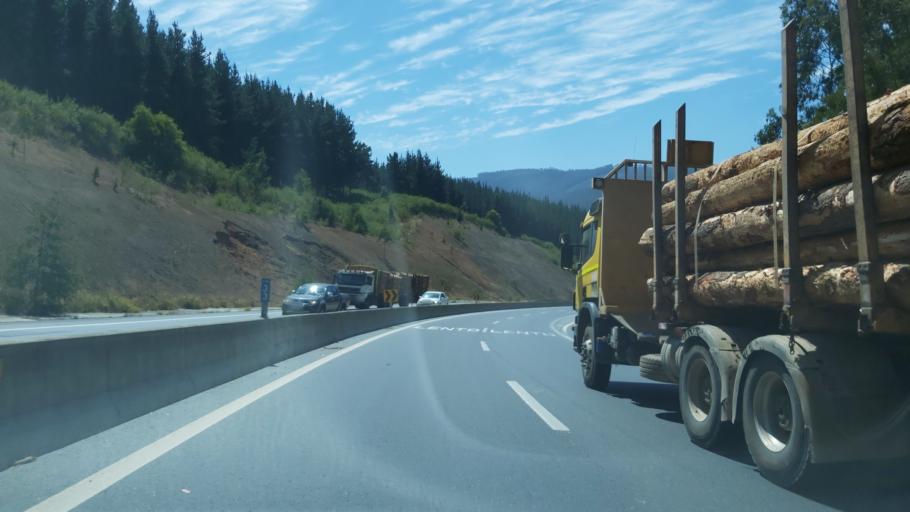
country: CL
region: Biobio
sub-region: Provincia de Concepcion
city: Lota
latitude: -37.1010
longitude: -73.1442
